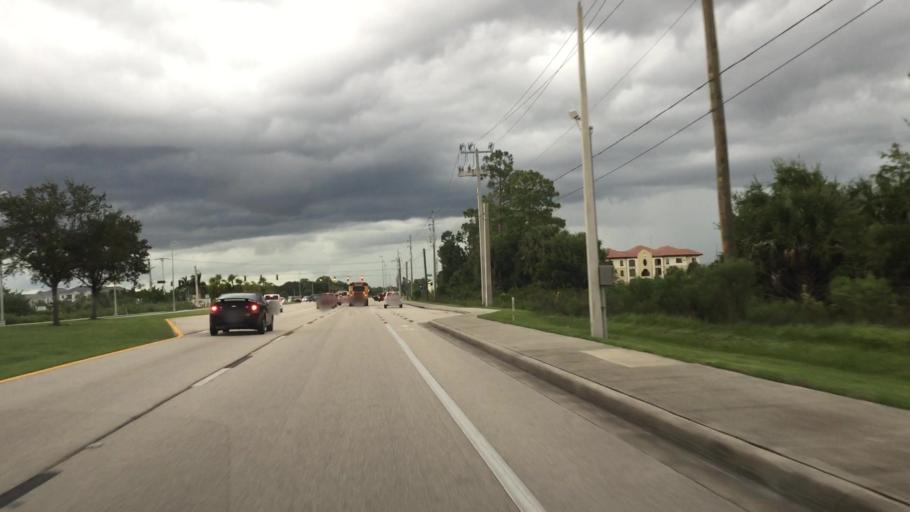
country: US
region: Florida
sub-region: Lee County
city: Estero
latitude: 26.4475
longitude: -81.7887
